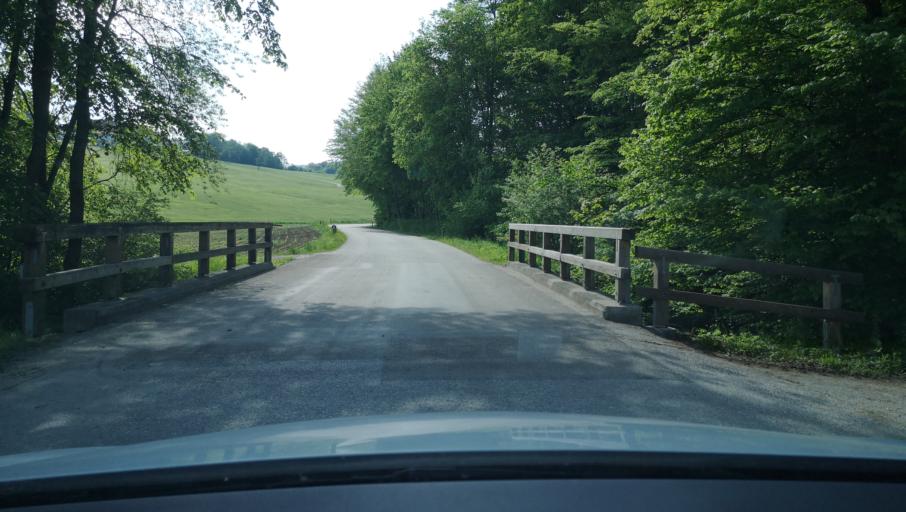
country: AT
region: Lower Austria
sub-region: Politischer Bezirk Amstetten
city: Neuhofen an der Ybbs
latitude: 48.0522
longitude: 14.8797
